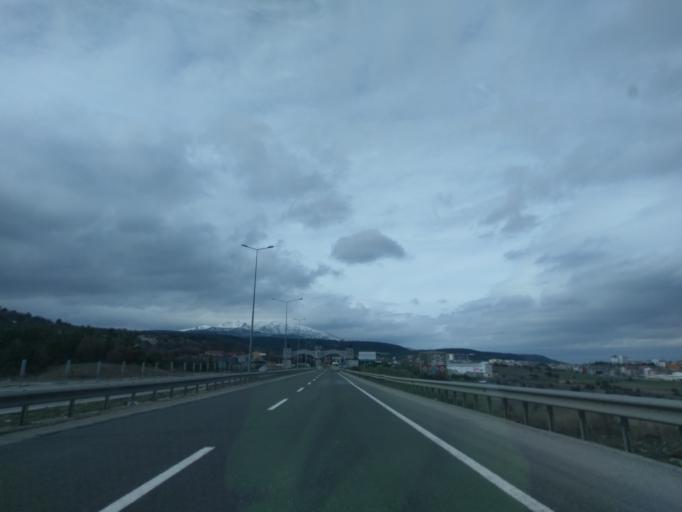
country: TR
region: Kuetahya
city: Kutahya
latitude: 39.3758
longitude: 30.0602
